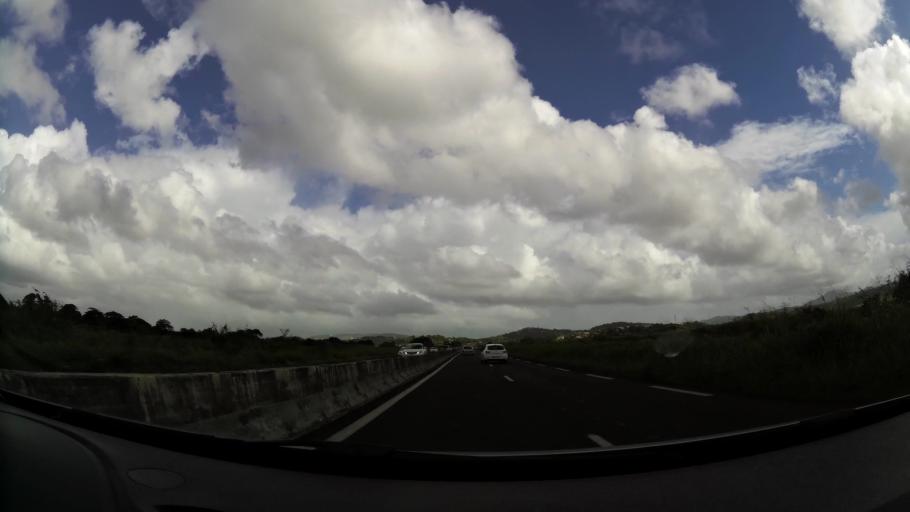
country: MQ
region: Martinique
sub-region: Martinique
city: Ducos
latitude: 14.5394
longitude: -60.9786
